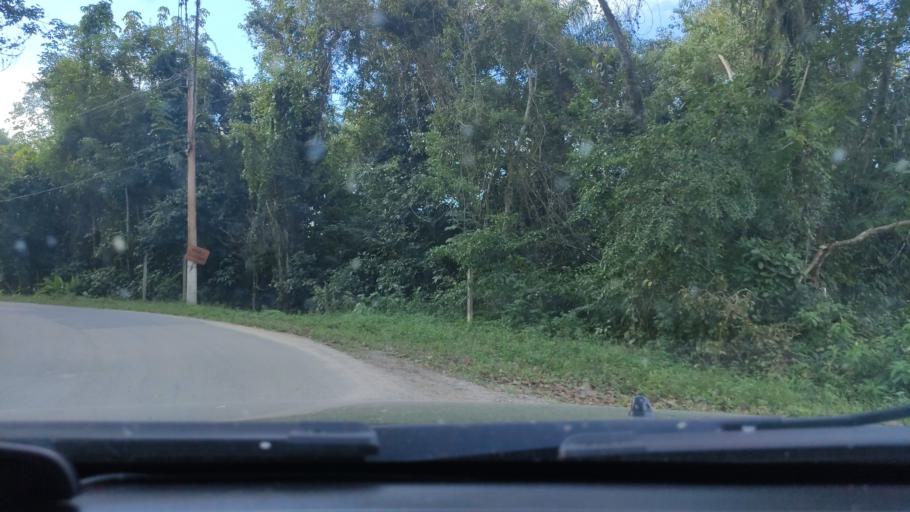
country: BR
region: Sao Paulo
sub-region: Sao Sebastiao
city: Sao Sebastiao
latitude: -23.6958
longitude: -45.4626
